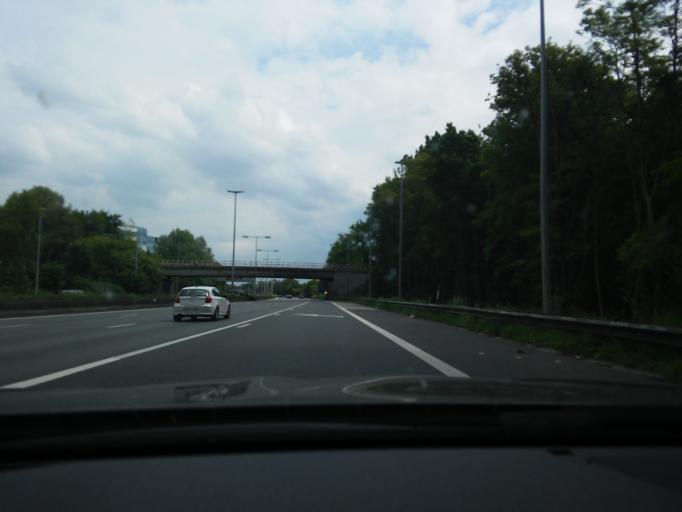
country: BE
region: Flanders
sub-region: Provincie Oost-Vlaanderen
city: Aalst
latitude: 50.9166
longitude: 4.0360
